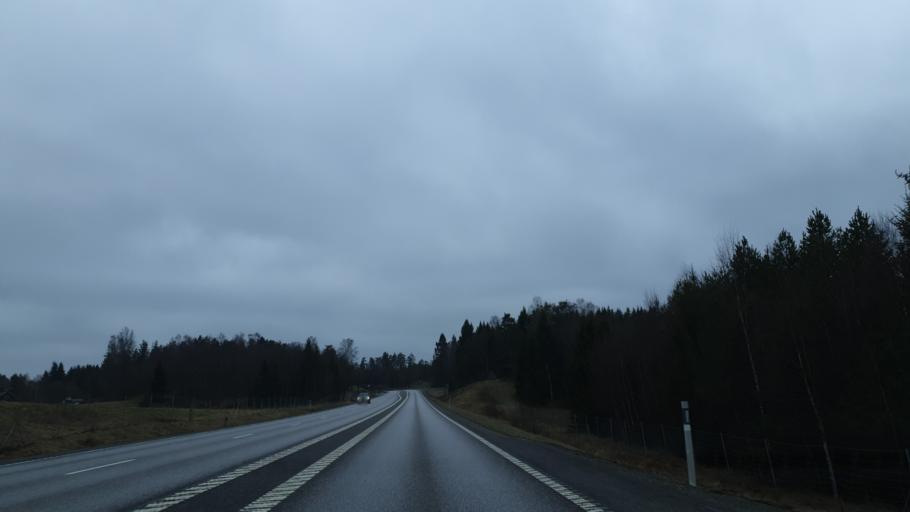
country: SE
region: Vaestra Goetaland
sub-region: Boras Kommun
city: Viskafors
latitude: 57.5982
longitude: 12.8701
